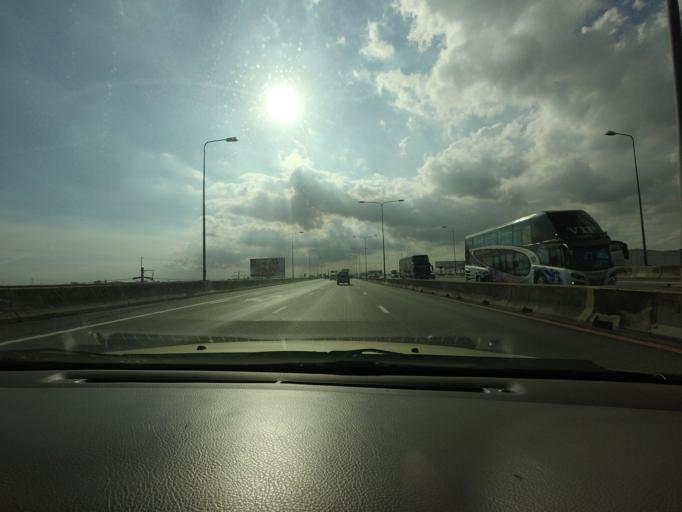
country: TH
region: Samut Prakan
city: Bang Bo District
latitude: 13.6179
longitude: 100.7442
